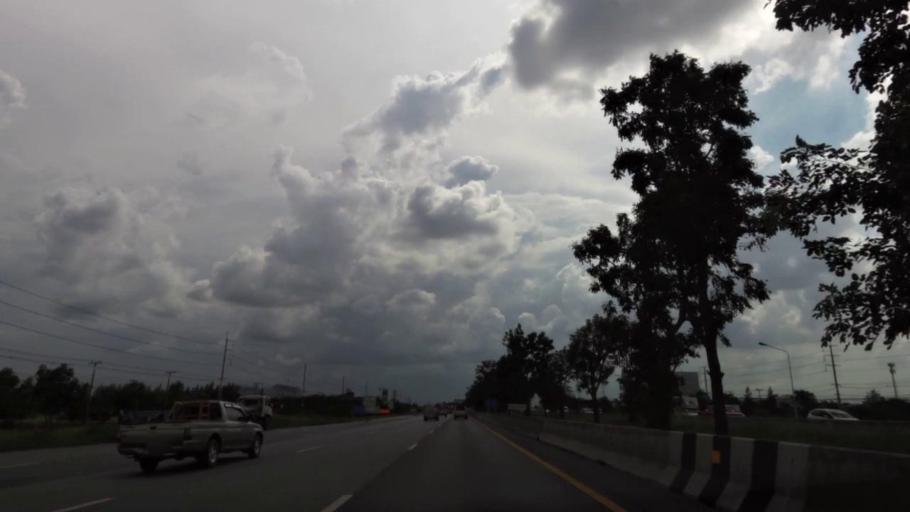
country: TH
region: Phra Nakhon Si Ayutthaya
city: Bang Pa-in
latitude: 14.2165
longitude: 100.6098
